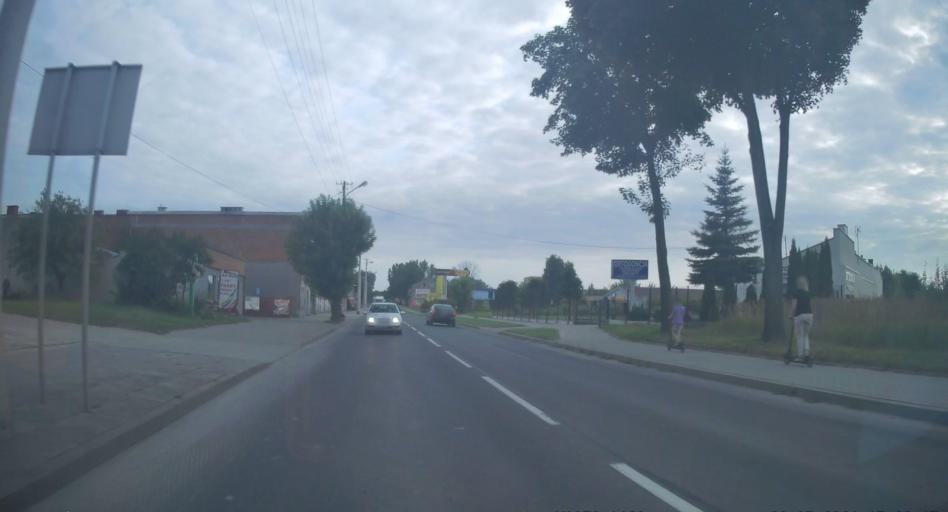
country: PL
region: Lodz Voivodeship
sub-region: Powiat radomszczanski
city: Radomsko
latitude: 51.0752
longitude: 19.4481
